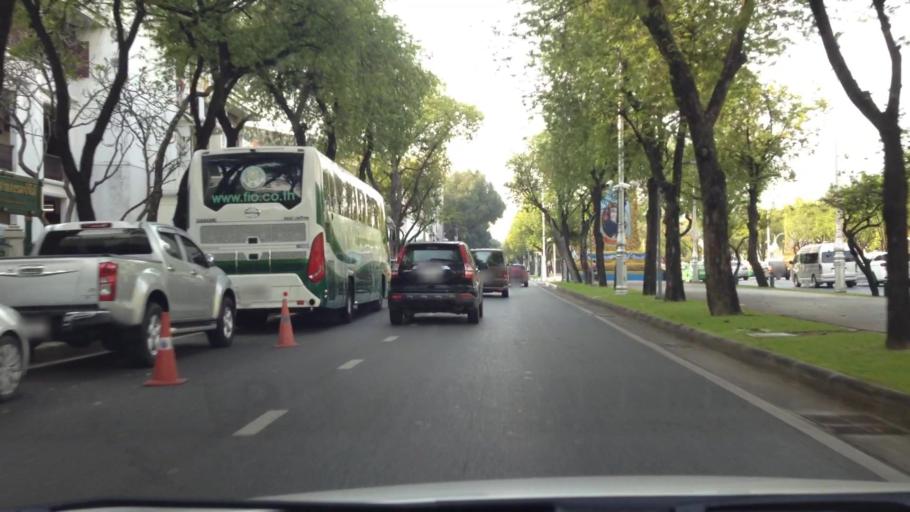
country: TH
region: Bangkok
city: Pom Prap Sattru Phai
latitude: 13.7622
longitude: 100.5089
